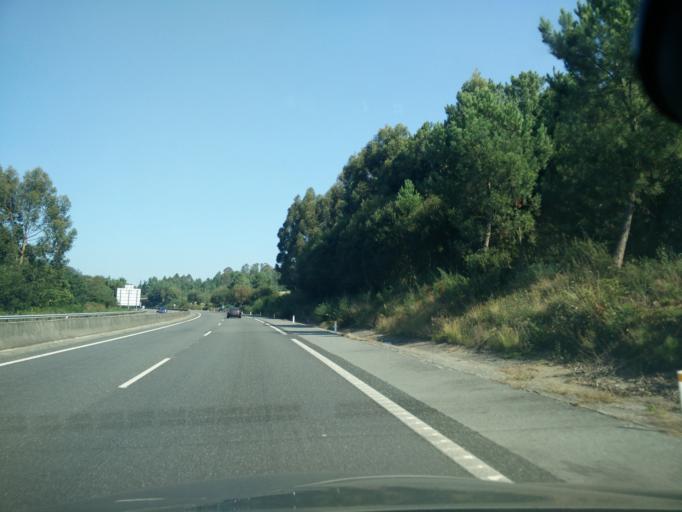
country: ES
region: Galicia
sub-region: Provincia da Coruna
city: Mino
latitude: 43.3832
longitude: -8.1783
